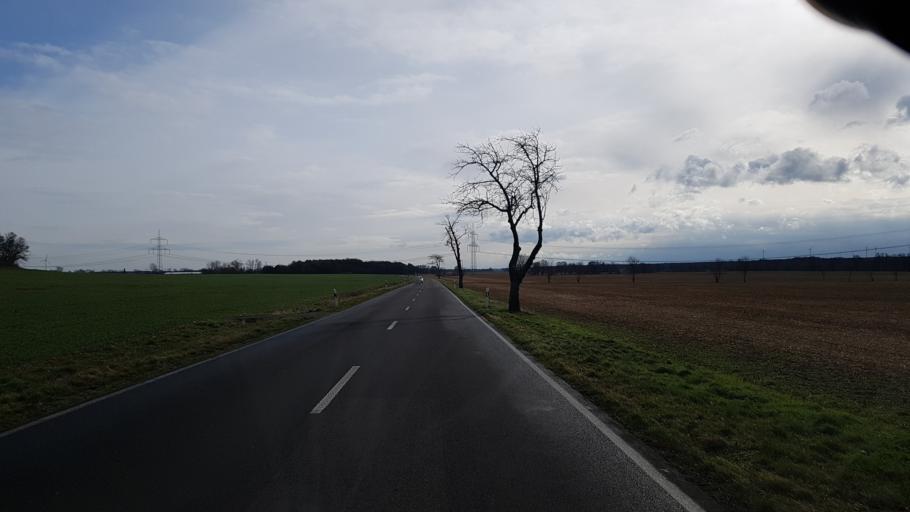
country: DE
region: Brandenburg
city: Schlieben
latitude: 51.7169
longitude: 13.3919
